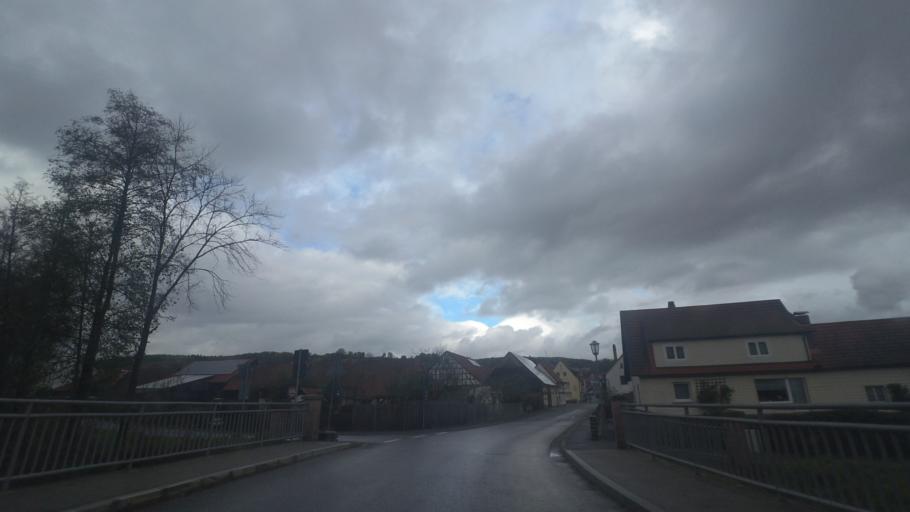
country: DE
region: Bavaria
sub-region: Regierungsbezirk Unterfranken
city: Oberelsbach
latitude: 50.3797
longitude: 10.1035
